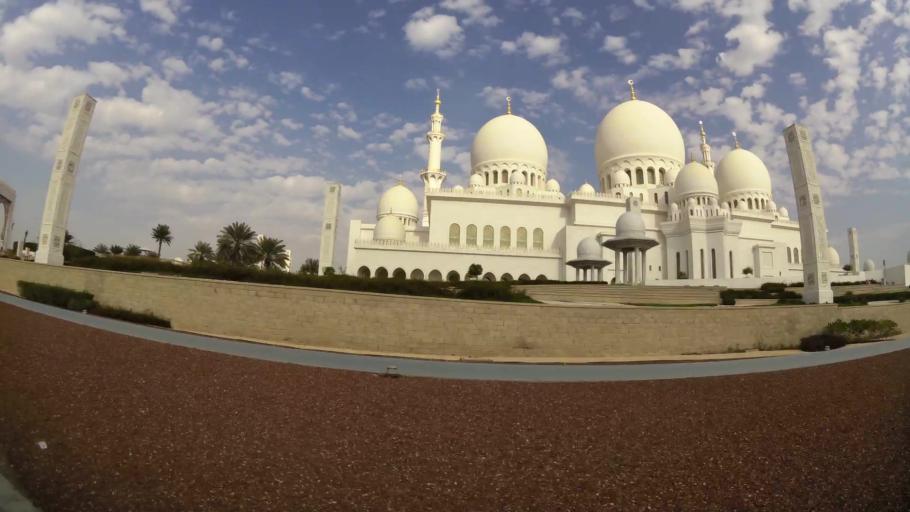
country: AE
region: Abu Dhabi
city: Abu Dhabi
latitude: 24.4126
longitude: 54.4721
